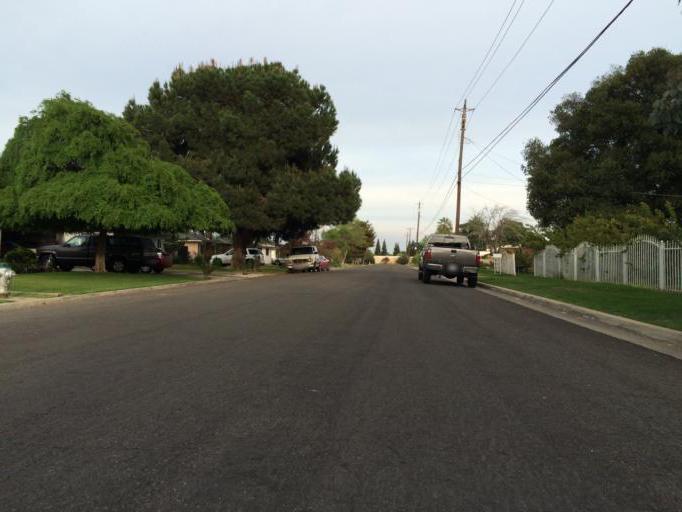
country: US
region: California
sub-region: Fresno County
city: Tarpey Village
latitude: 36.7759
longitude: -119.7342
